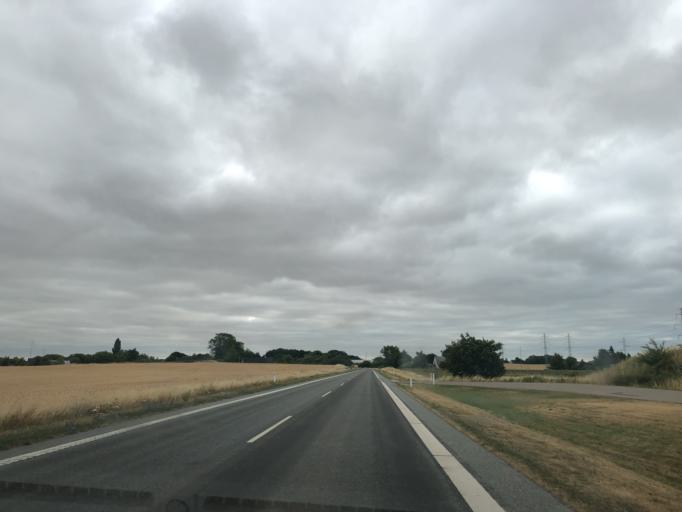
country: DK
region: Zealand
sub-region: Slagelse Kommune
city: Skaelskor
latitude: 55.2167
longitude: 11.2901
